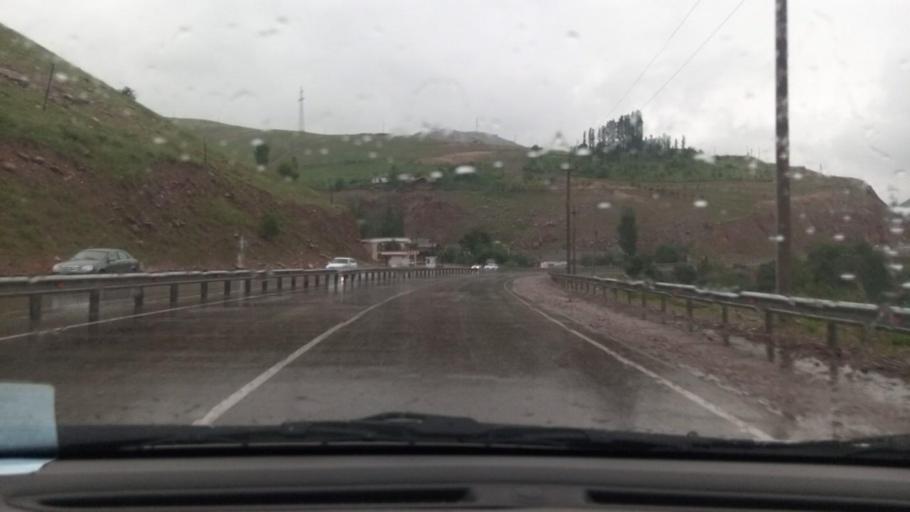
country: UZ
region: Toshkent
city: Angren
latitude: 41.1017
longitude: 70.3298
